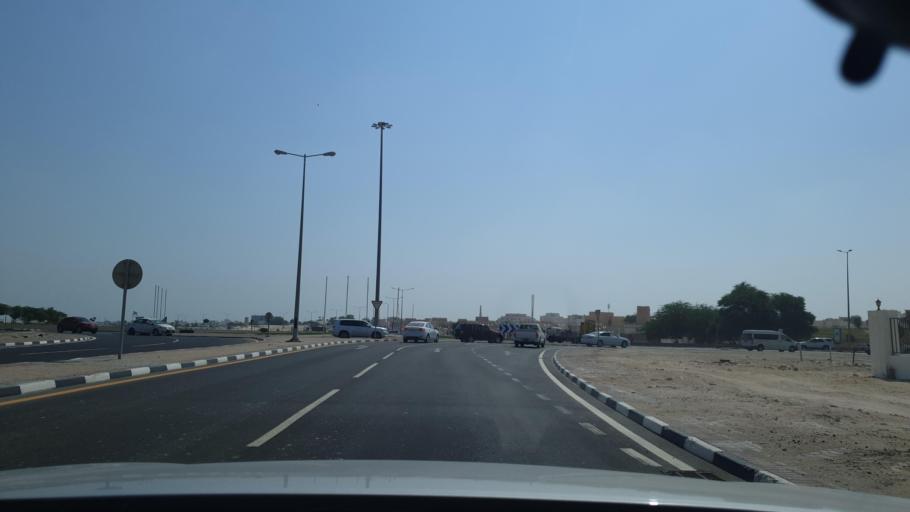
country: QA
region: Al Khawr
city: Al Khawr
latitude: 25.6913
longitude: 51.4992
